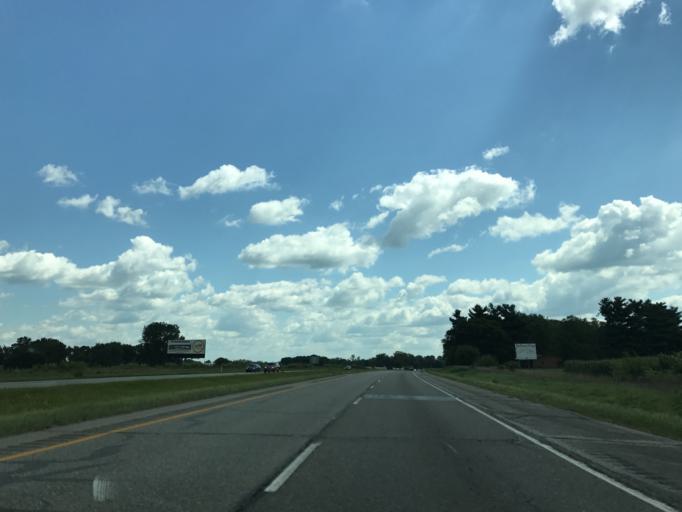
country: US
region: Indiana
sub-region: Marshall County
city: Plymouth
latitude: 41.3621
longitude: -86.3007
